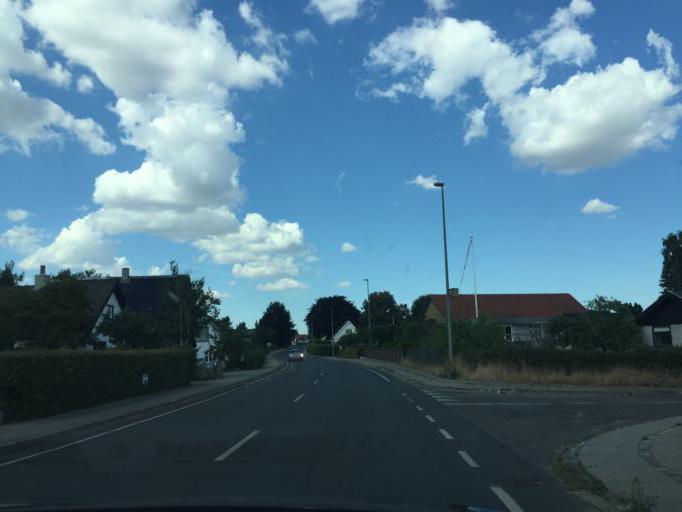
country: DK
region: South Denmark
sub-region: Assens Kommune
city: Harby
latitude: 55.2180
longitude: 10.1201
